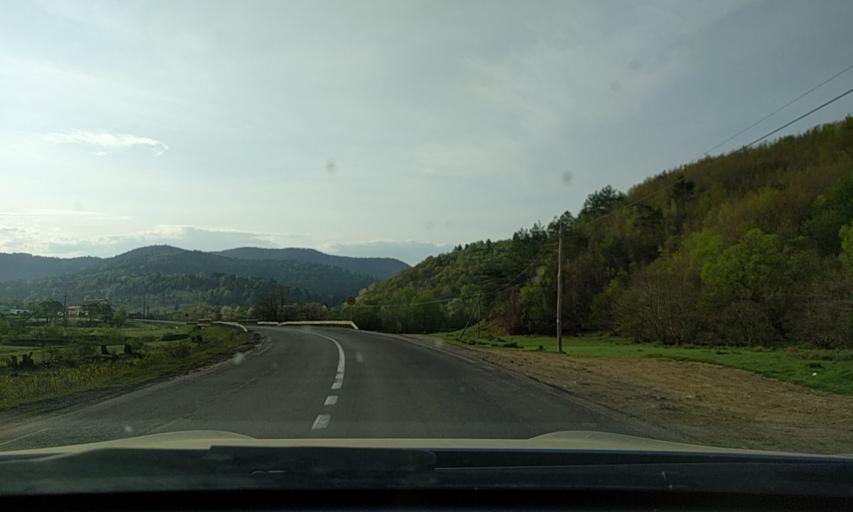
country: RO
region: Covasna
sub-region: Comuna Bretcu
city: Bretcu
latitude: 46.0467
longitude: 26.3209
